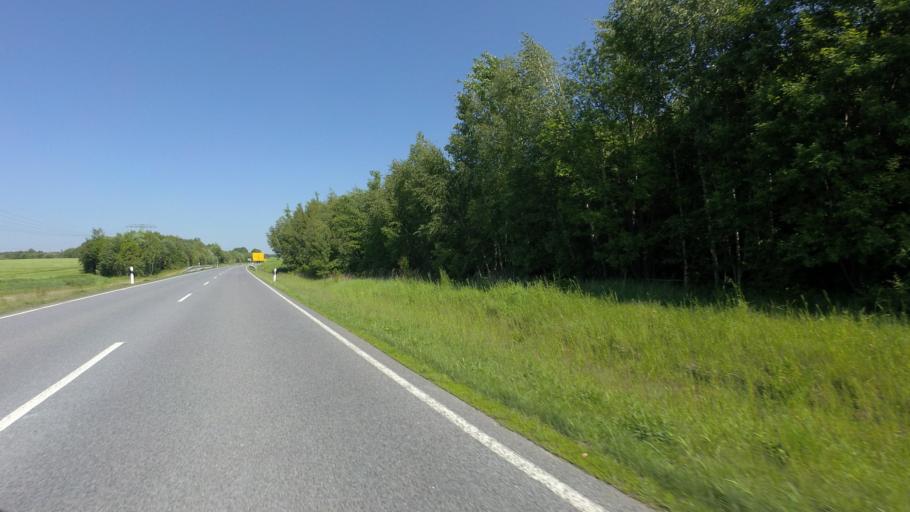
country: DE
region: Saxony
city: Nebelschutz
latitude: 51.2616
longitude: 14.1495
